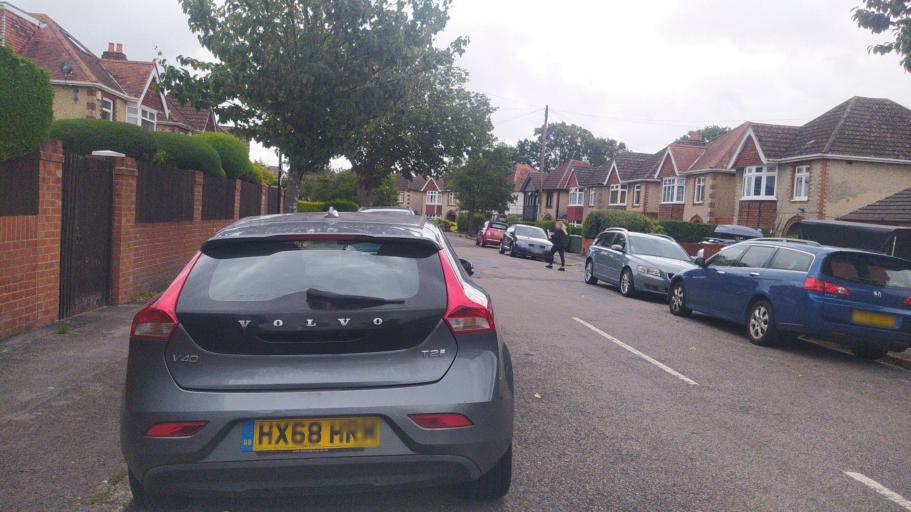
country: GB
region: England
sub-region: Hampshire
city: West End
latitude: 50.9092
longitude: -1.3554
